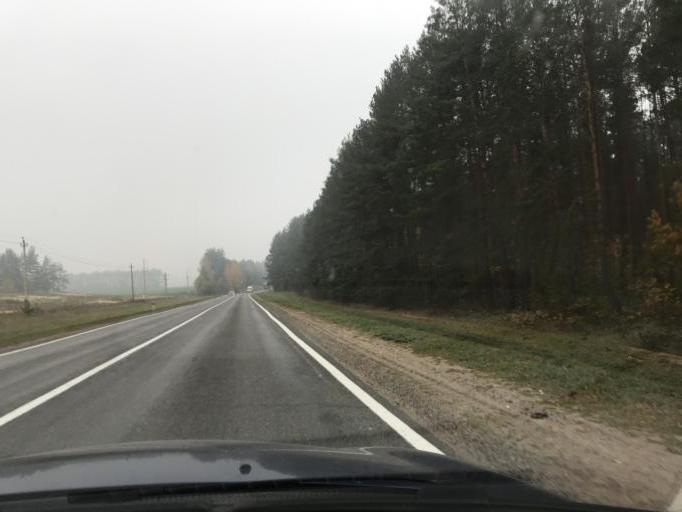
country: BY
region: Grodnenskaya
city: Hrodna
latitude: 53.7855
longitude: 23.8513
